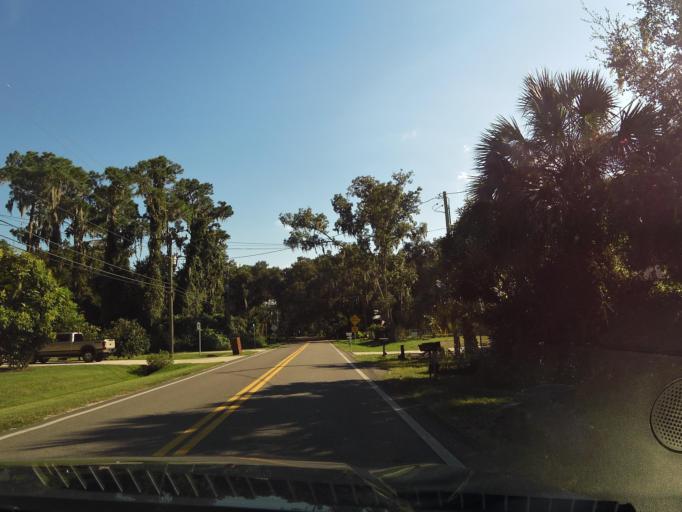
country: US
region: Florida
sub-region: Putnam County
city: East Palatka
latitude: 29.8437
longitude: -81.5587
